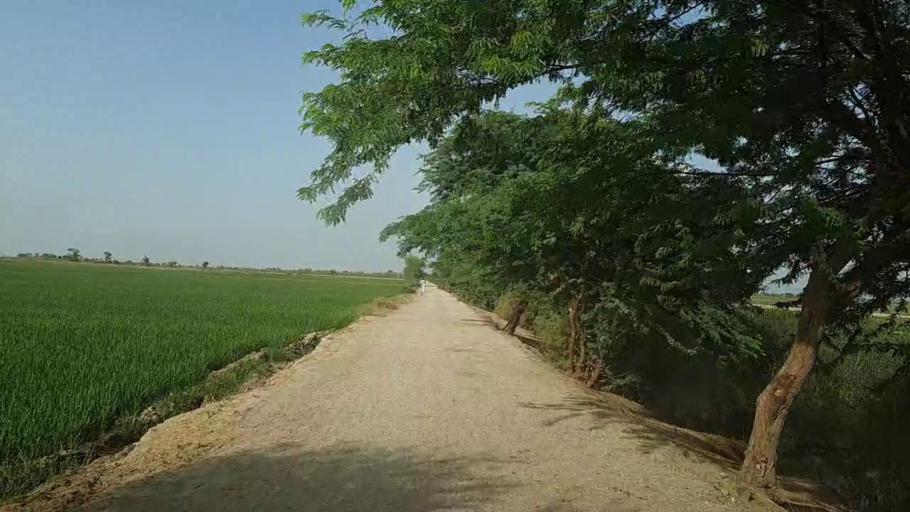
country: PK
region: Sindh
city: Sita Road
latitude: 27.0936
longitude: 67.8689
